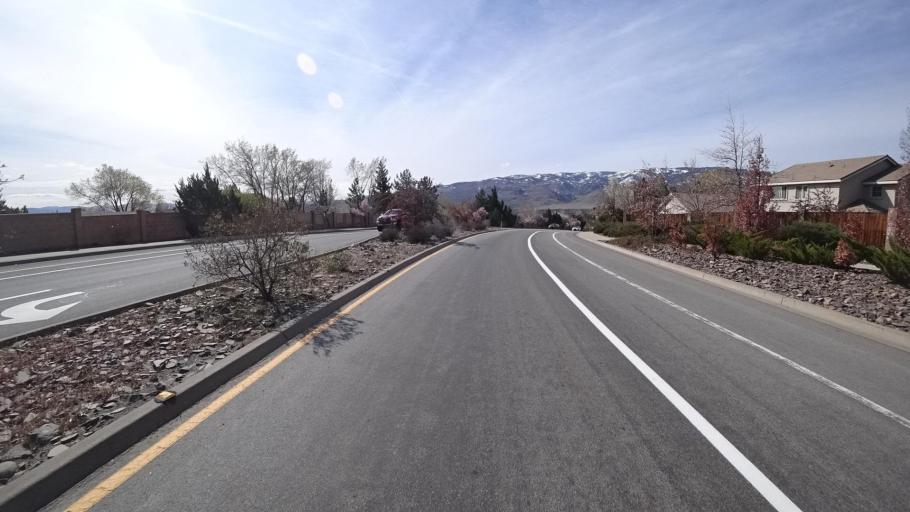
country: US
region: Nevada
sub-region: Washoe County
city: Mogul
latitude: 39.5300
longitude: -119.8935
